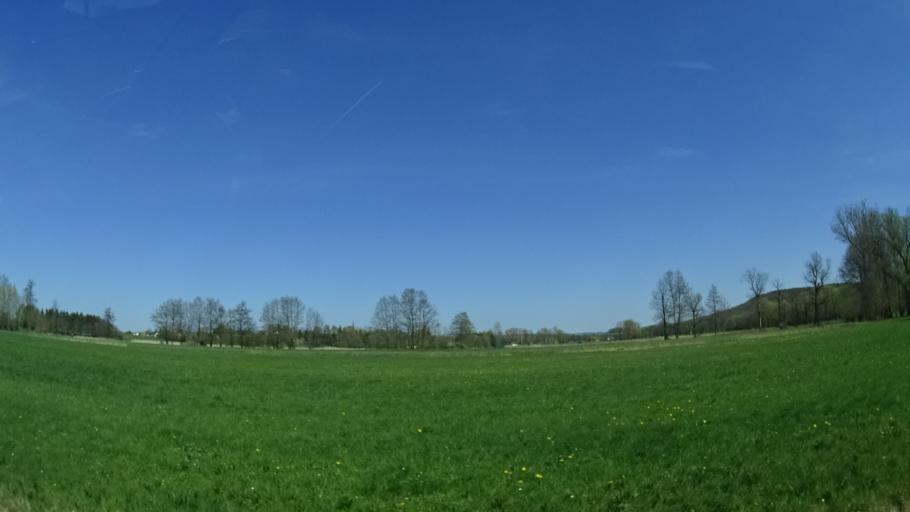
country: DE
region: Thuringia
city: Veilsdorf
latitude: 50.3010
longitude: 10.7947
